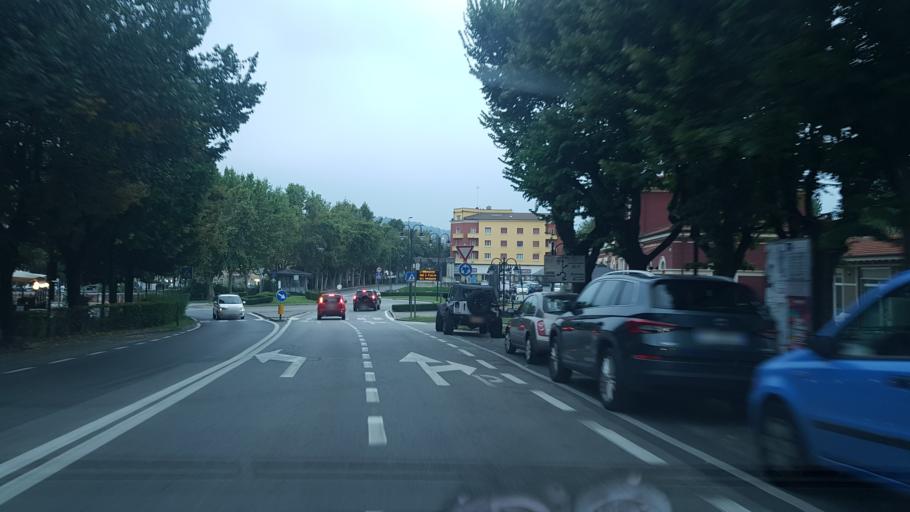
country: IT
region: Piedmont
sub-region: Provincia di Cuneo
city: Mondovi
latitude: 44.3908
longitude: 7.8193
